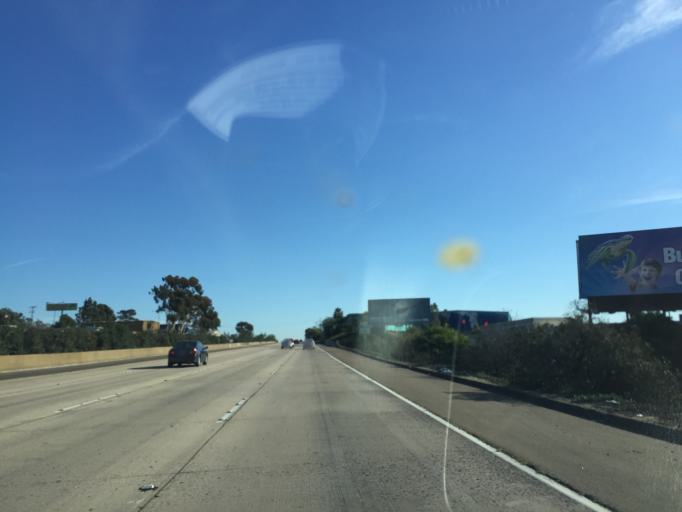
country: US
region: California
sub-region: San Diego County
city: La Jolla
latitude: 32.8104
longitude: -117.2190
